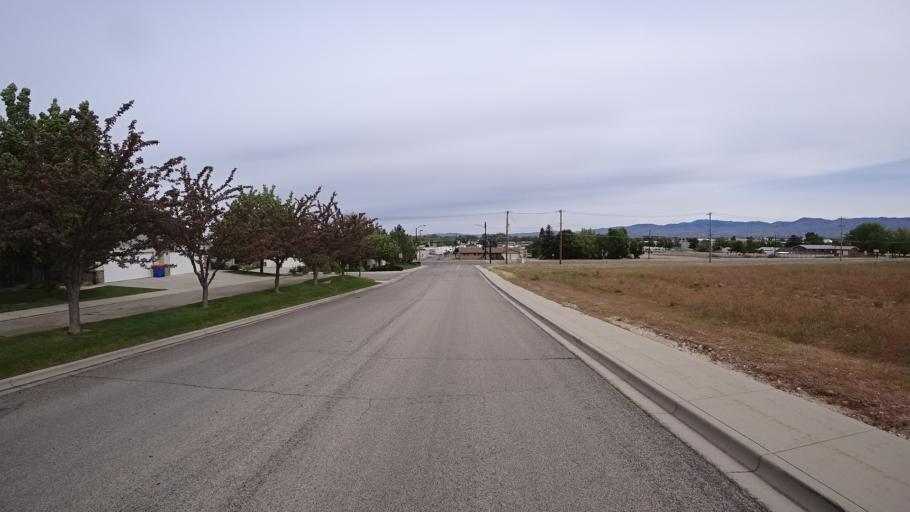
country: US
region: Idaho
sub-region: Ada County
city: Garden City
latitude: 43.5747
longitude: -116.2866
